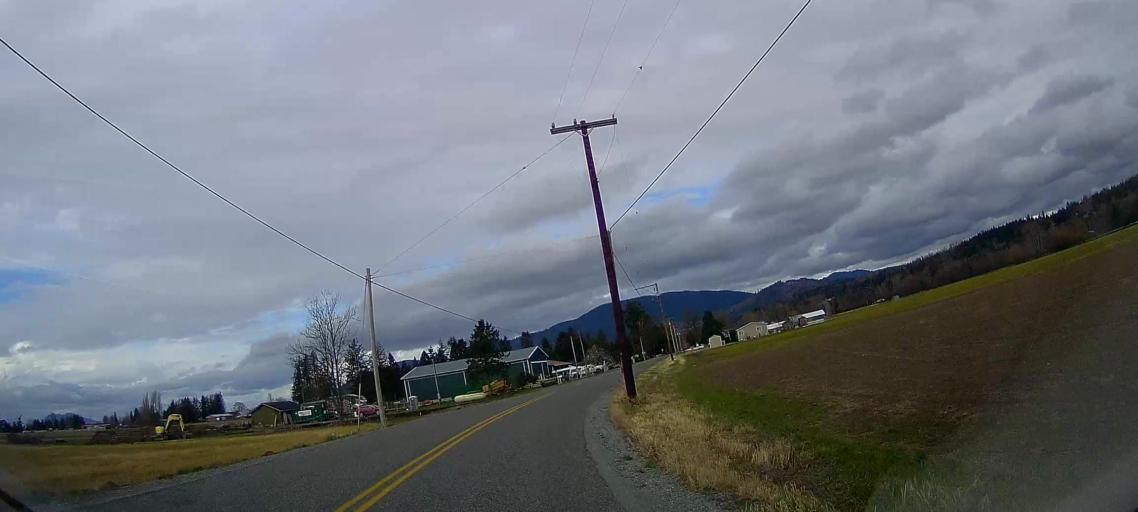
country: US
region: Washington
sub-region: Skagit County
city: Burlington
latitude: 48.5521
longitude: -122.4004
